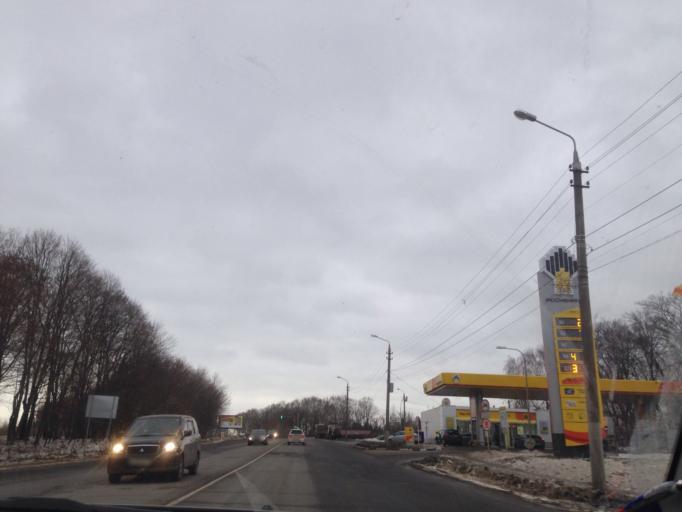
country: RU
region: Tula
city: Tula
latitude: 54.1545
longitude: 37.6383
